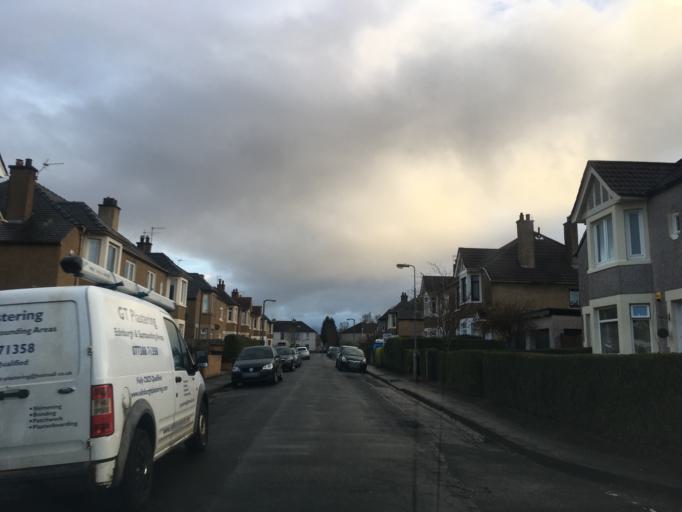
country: GB
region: Scotland
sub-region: Edinburgh
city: Colinton
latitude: 55.9404
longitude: -3.2569
